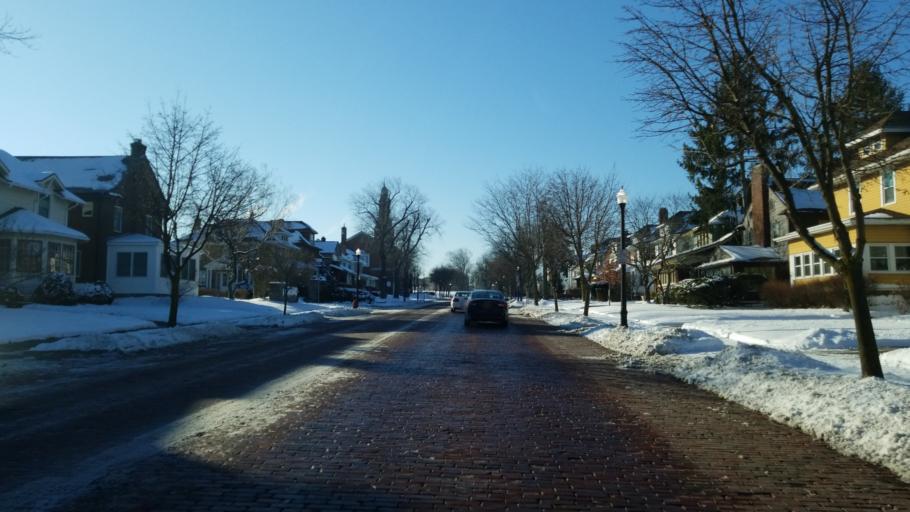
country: US
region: New York
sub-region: Erie County
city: Eggertsville
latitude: 42.9562
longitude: -78.8234
